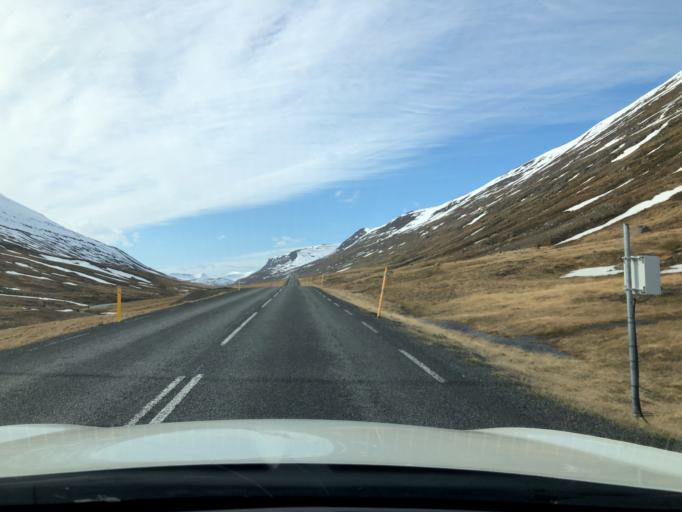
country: IS
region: East
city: Egilsstadir
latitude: 65.1685
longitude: -14.3383
